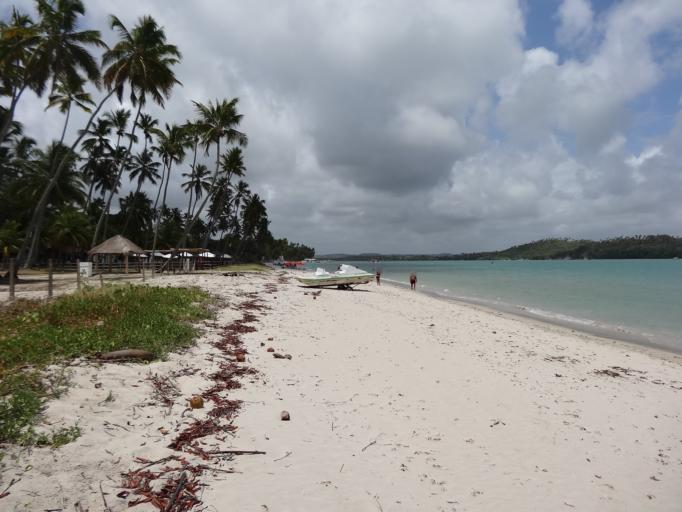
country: BR
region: Pernambuco
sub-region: Tamandare
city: Tamandare
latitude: -8.6984
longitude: -35.0864
